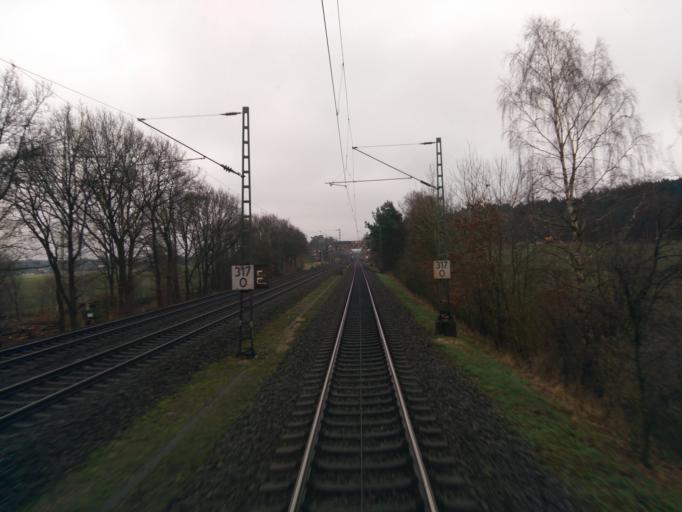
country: DE
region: Lower Saxony
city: Kakenstorf
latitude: 53.3012
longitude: 9.7950
